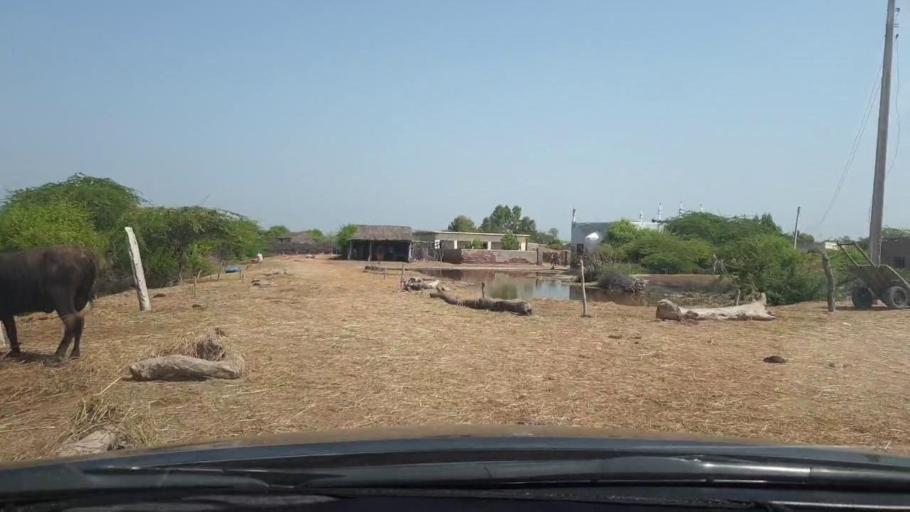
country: PK
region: Sindh
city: Tando Bago
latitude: 24.7892
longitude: 69.0829
